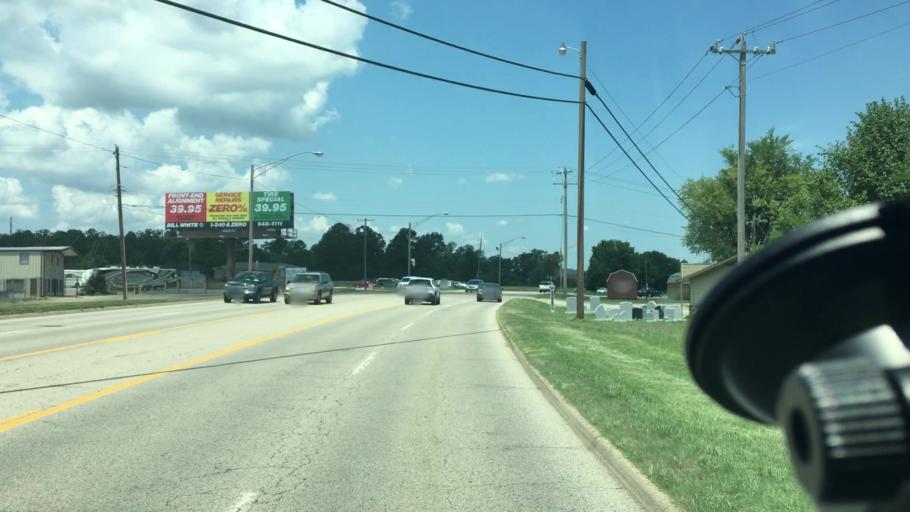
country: US
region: Arkansas
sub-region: Sebastian County
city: Barling
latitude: 35.3367
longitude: -94.3179
